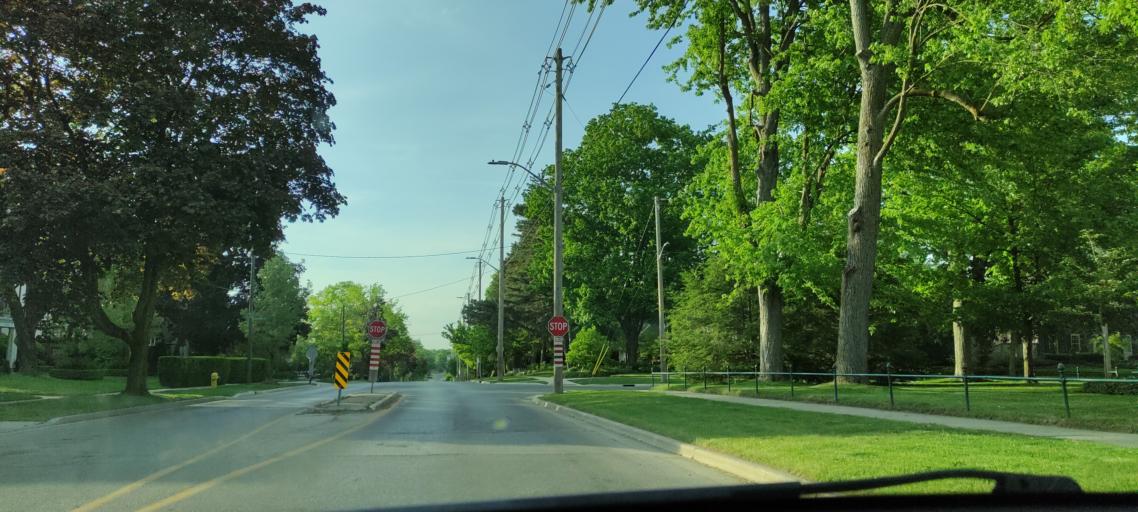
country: CA
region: Ontario
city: London
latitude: 43.0007
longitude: -81.2583
